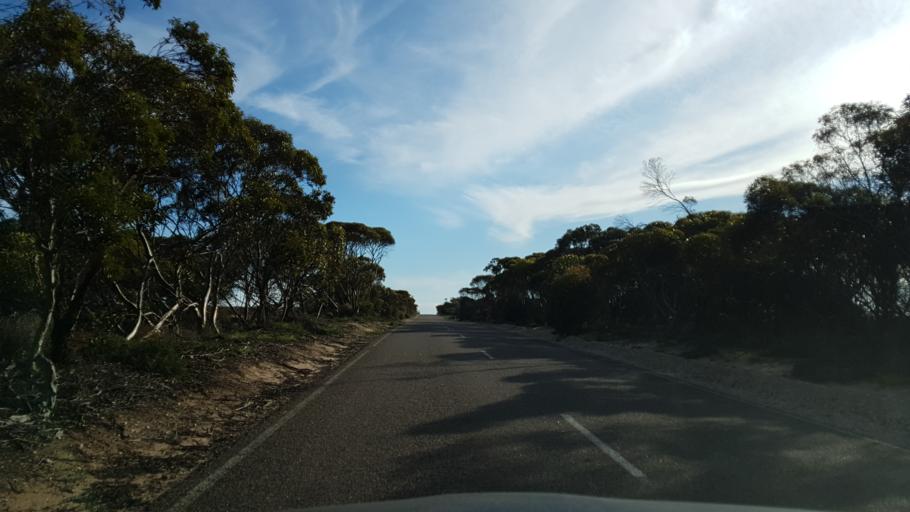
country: AU
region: South Australia
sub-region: Murray Bridge
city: Tailem Bend
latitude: -35.0647
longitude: 139.4652
